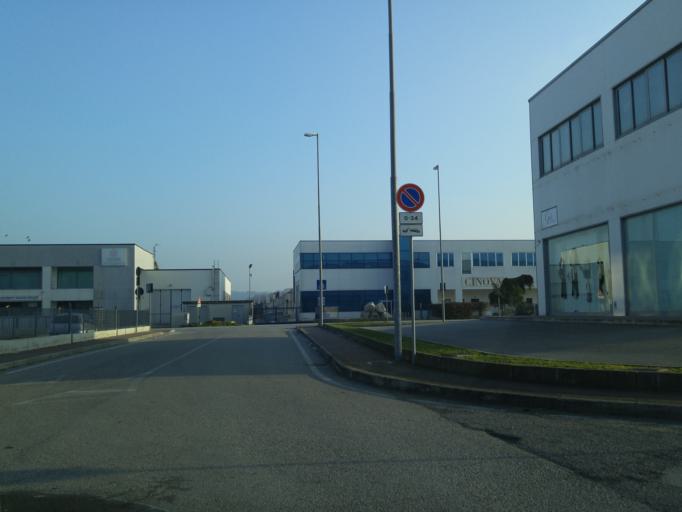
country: IT
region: The Marches
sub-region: Provincia di Pesaro e Urbino
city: Bellocchi
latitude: 43.7931
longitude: 13.0019
